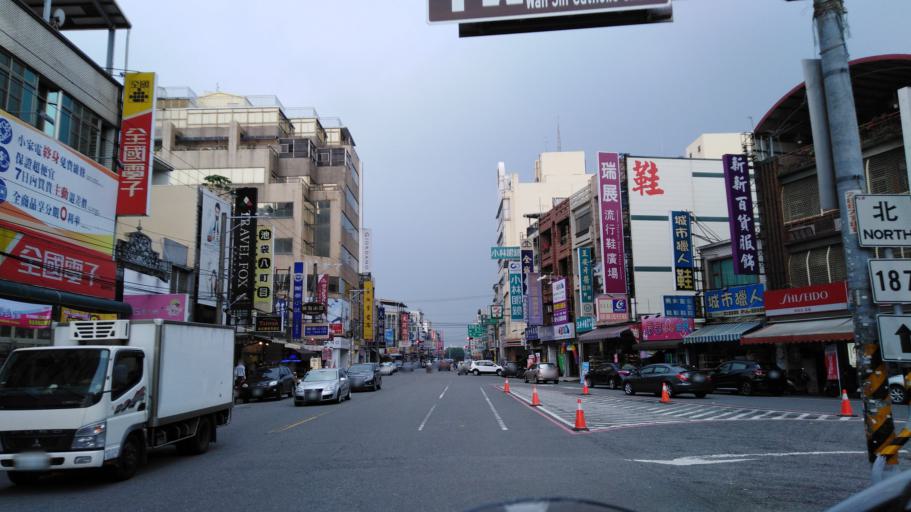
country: TW
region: Taiwan
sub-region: Pingtung
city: Pingtung
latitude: 22.5495
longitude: 120.5389
